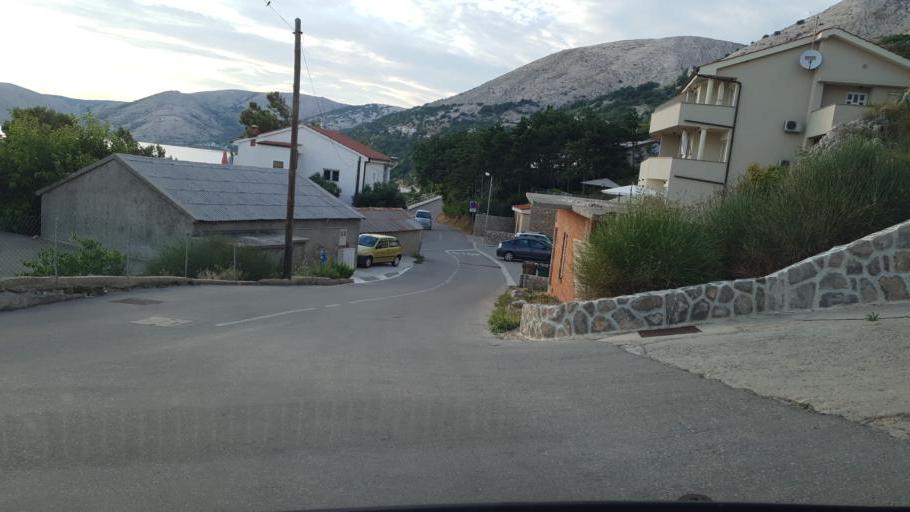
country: HR
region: Primorsko-Goranska
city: Punat
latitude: 44.9533
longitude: 14.6903
